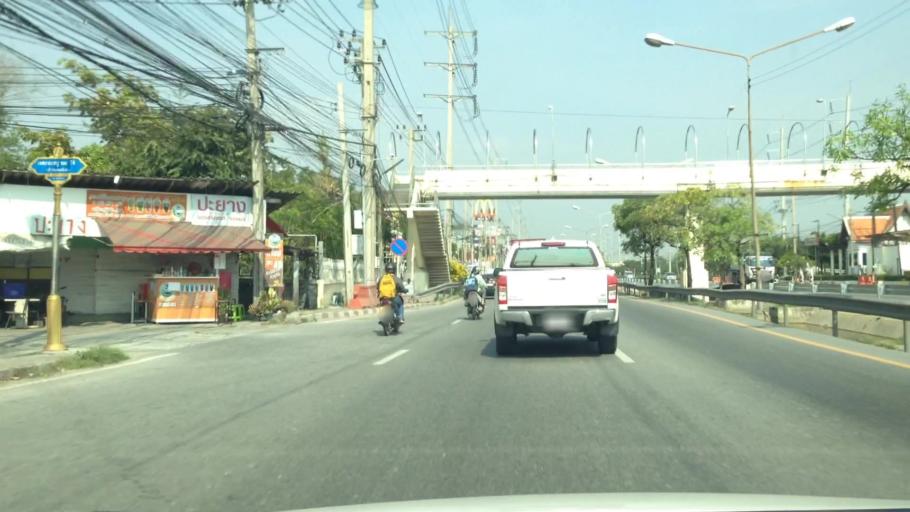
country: TH
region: Samut Prakan
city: Samut Prakan
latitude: 13.5395
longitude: 100.6211
